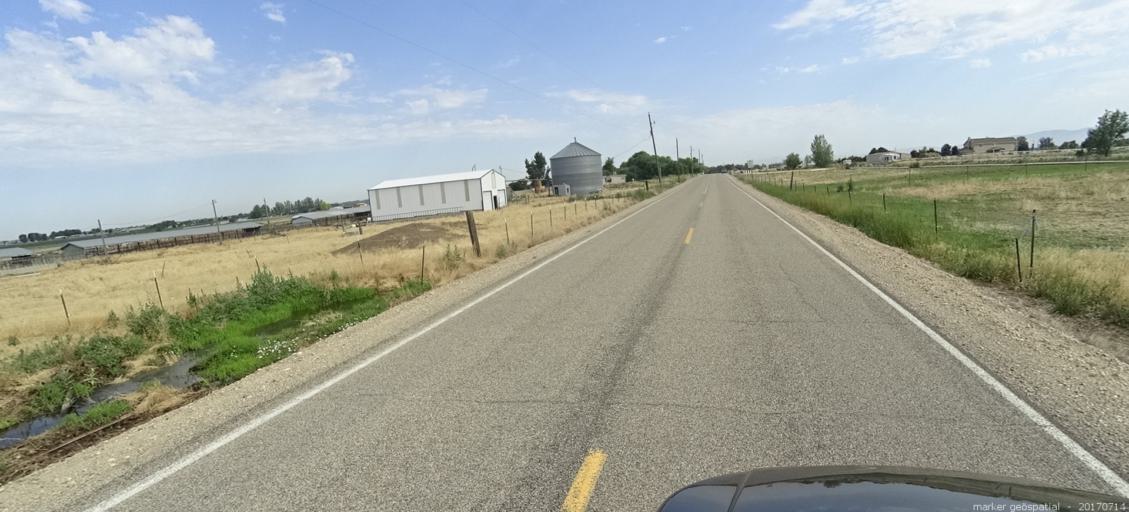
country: US
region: Idaho
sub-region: Ada County
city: Kuna
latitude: 43.4961
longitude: -116.3543
